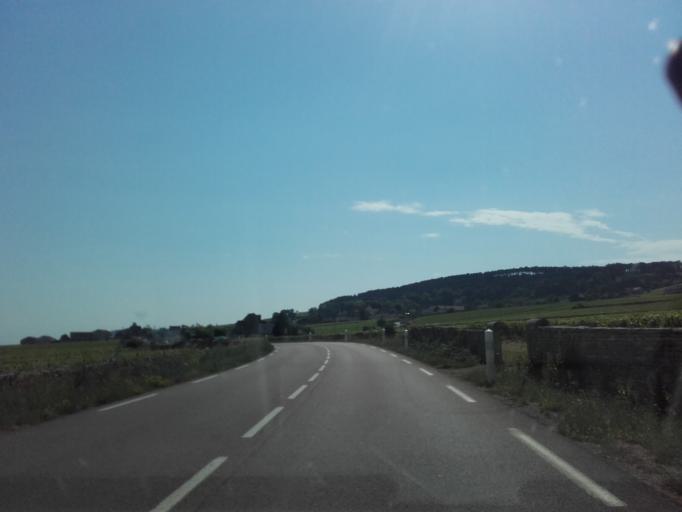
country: FR
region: Bourgogne
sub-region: Departement de la Cote-d'Or
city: Meursault
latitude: 47.0038
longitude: 4.7911
